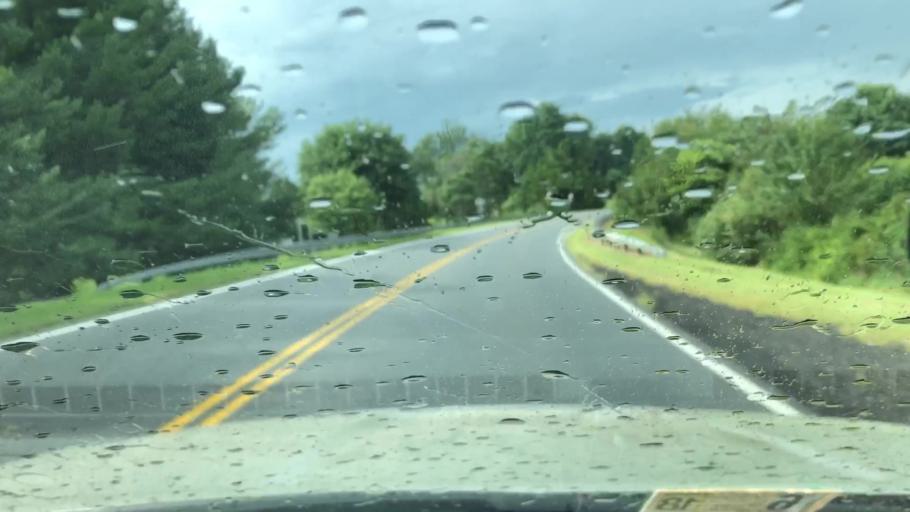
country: US
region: Virginia
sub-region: City of Waynesboro
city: Waynesboro
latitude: 38.0838
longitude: -78.9003
